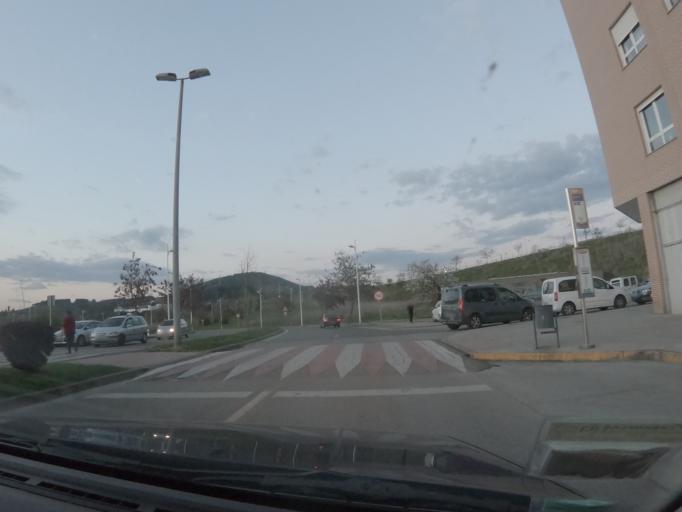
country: ES
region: Castille and Leon
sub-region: Provincia de Leon
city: Ponferrada
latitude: 42.5527
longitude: -6.5875
